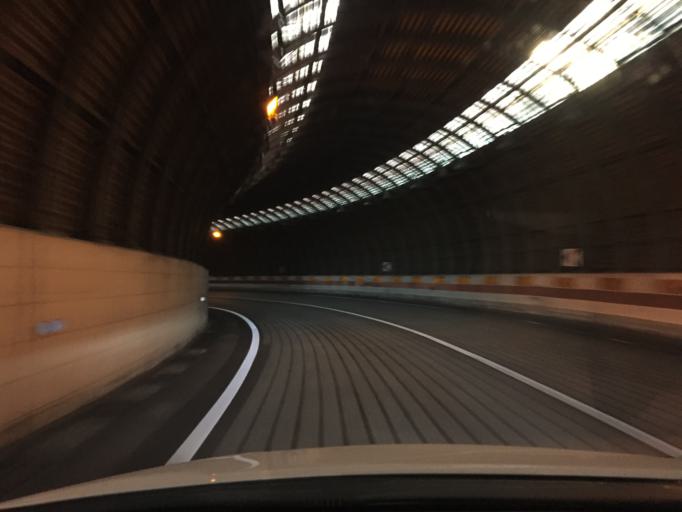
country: JP
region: Fukushima
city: Inawashiro
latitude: 37.6634
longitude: 140.0119
